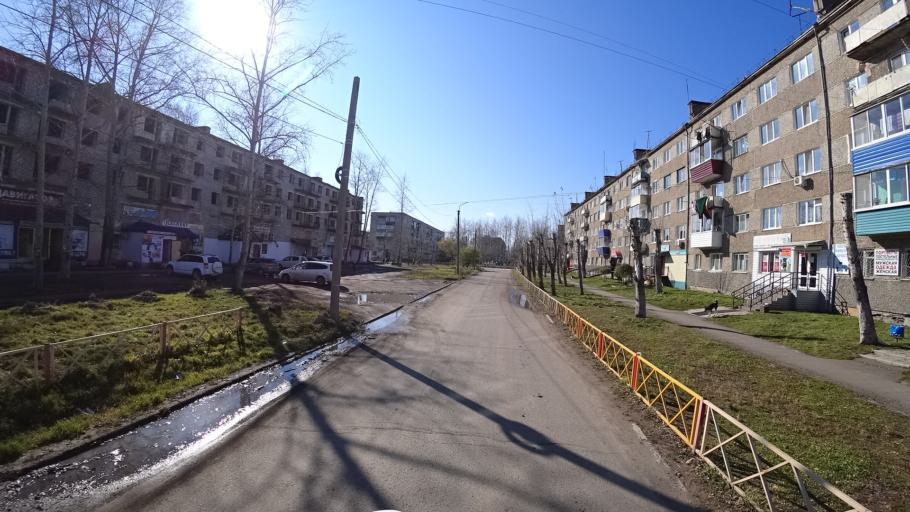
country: RU
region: Khabarovsk Krai
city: Amursk
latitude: 50.0998
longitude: 136.5130
